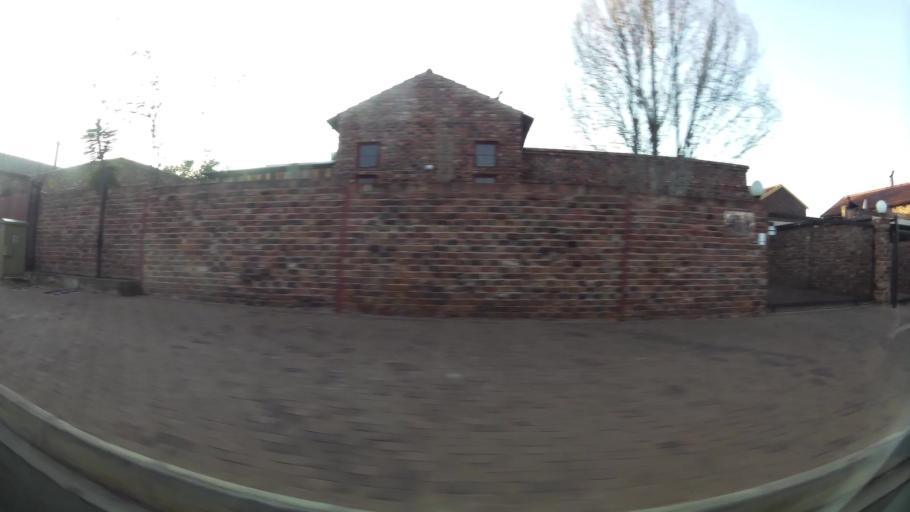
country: ZA
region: Orange Free State
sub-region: Mangaung Metropolitan Municipality
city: Bloemfontein
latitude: -29.1034
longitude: 26.1639
